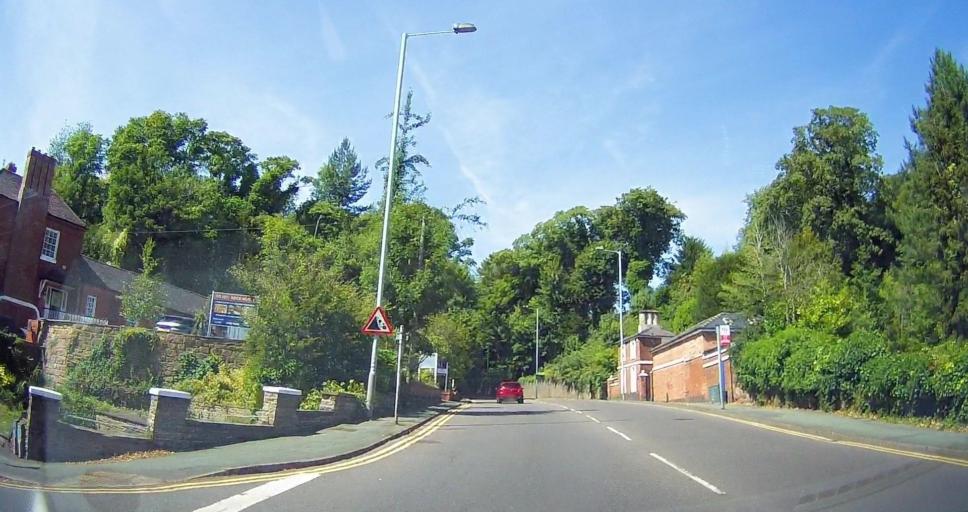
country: GB
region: England
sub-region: Wolverhampton
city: Wolverhampton
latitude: 52.5983
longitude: -2.1632
